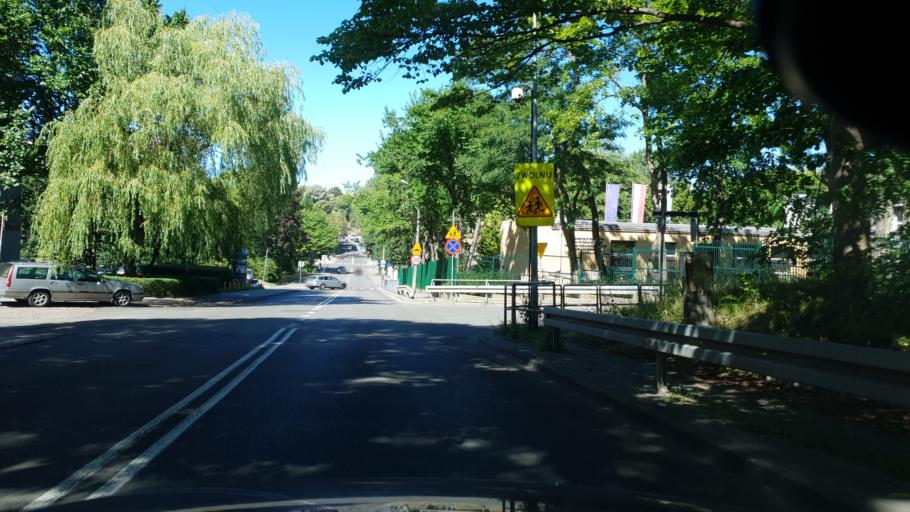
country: PL
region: Pomeranian Voivodeship
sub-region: Gdynia
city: Gdynia
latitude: 54.5067
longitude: 18.5442
